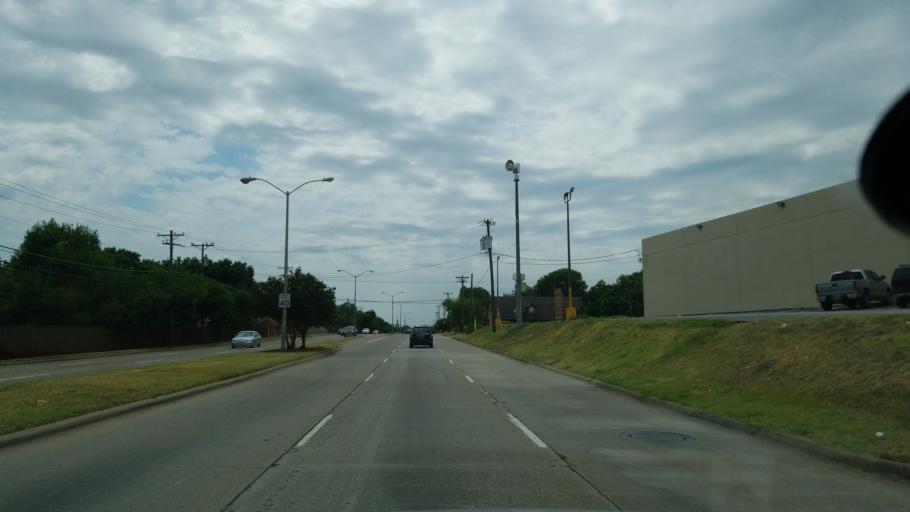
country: US
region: Texas
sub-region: Dallas County
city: Duncanville
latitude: 32.6708
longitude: -96.8572
